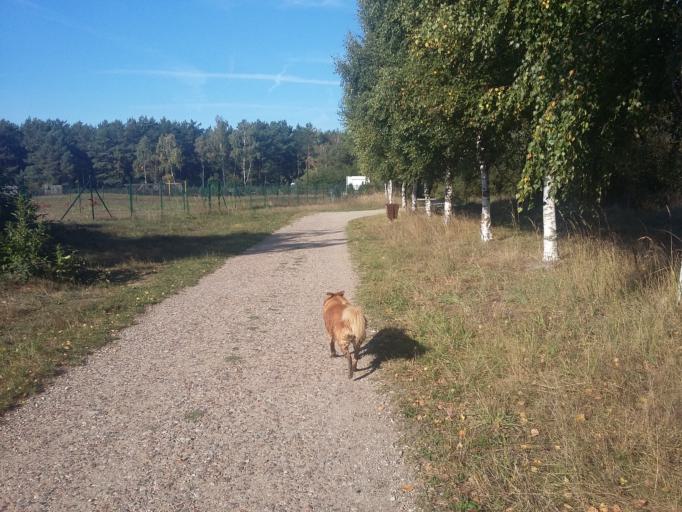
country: PL
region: Lodz Voivodeship
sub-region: Powiat pabianicki
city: Ksawerow
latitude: 51.7285
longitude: 19.3848
